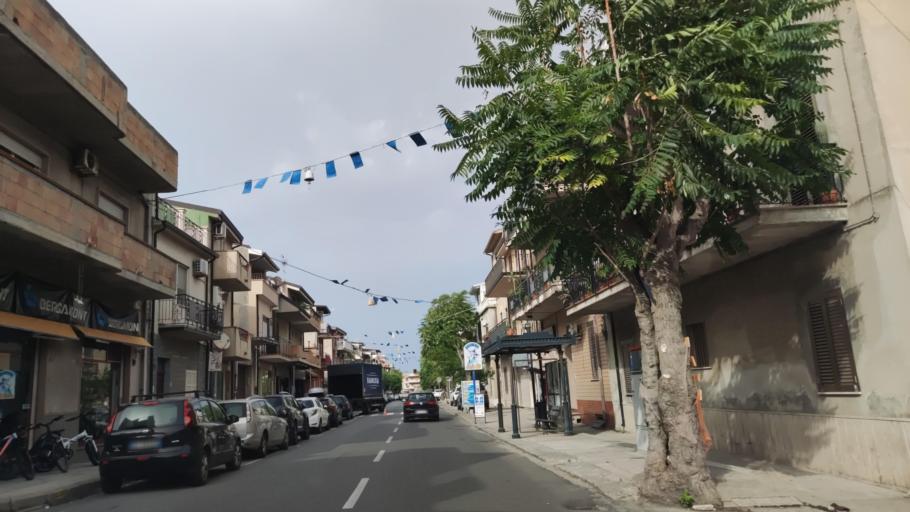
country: IT
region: Calabria
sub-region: Provincia di Reggio Calabria
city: Siderno
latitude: 38.2627
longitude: 16.2906
